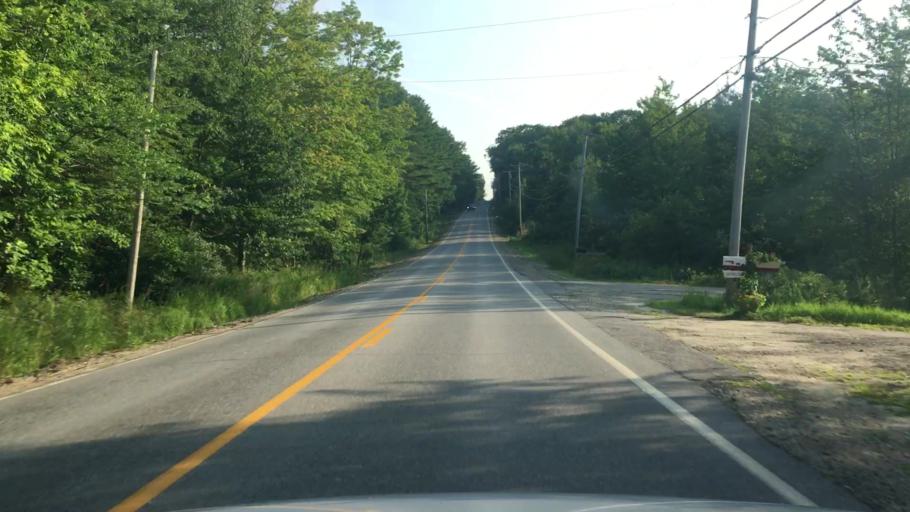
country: US
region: Maine
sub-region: Androscoggin County
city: Lisbon Falls
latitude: 43.9565
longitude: -70.0604
